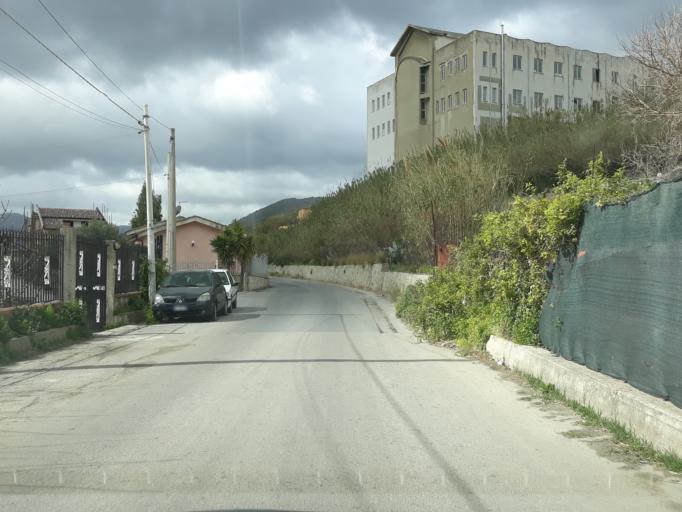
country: IT
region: Sicily
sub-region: Palermo
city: Monreale
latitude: 38.0803
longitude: 13.2948
